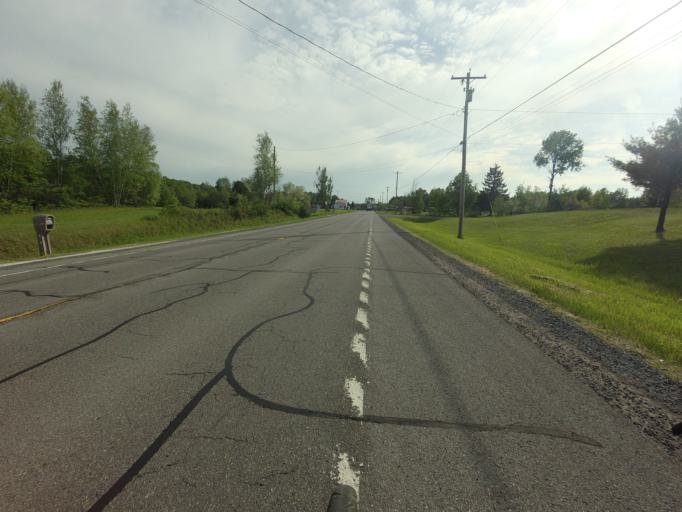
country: US
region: New York
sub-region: St. Lawrence County
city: Gouverneur
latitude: 44.1757
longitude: -75.2929
